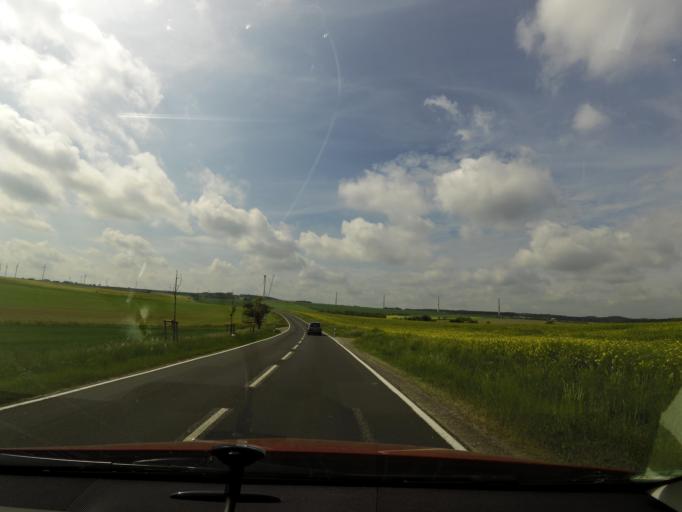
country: DE
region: Thuringia
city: Mihla
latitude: 51.0698
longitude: 10.3245
